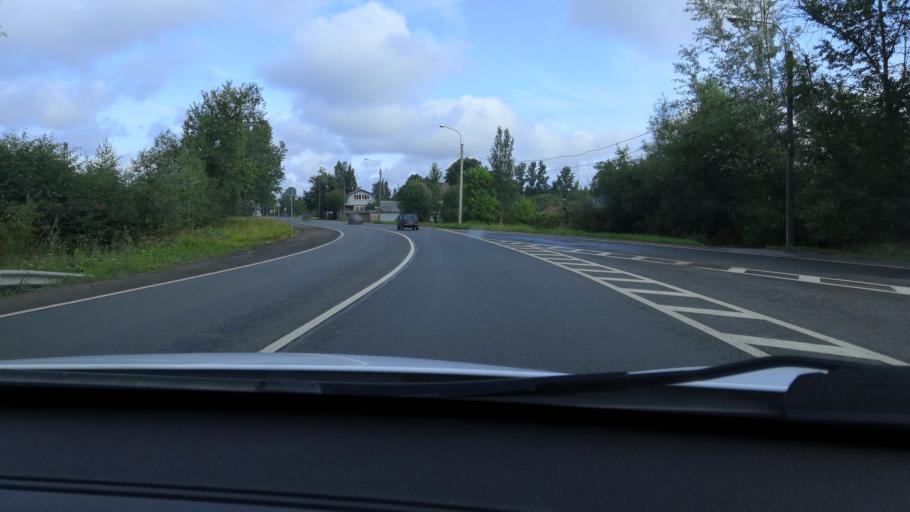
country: RU
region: St.-Petersburg
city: Tyarlevo
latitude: 59.7051
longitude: 30.4387
